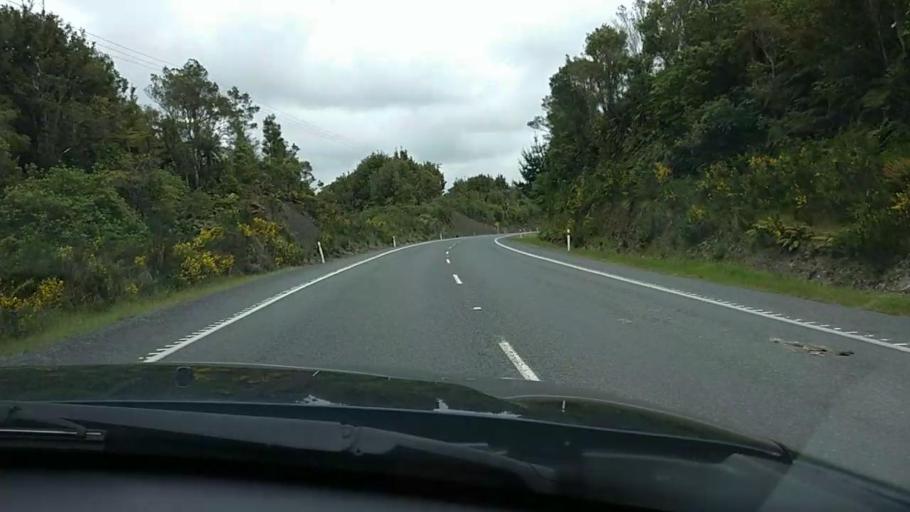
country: NZ
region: Bay of Plenty
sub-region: Rotorua District
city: Rotorua
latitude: -38.0719
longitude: 176.1227
